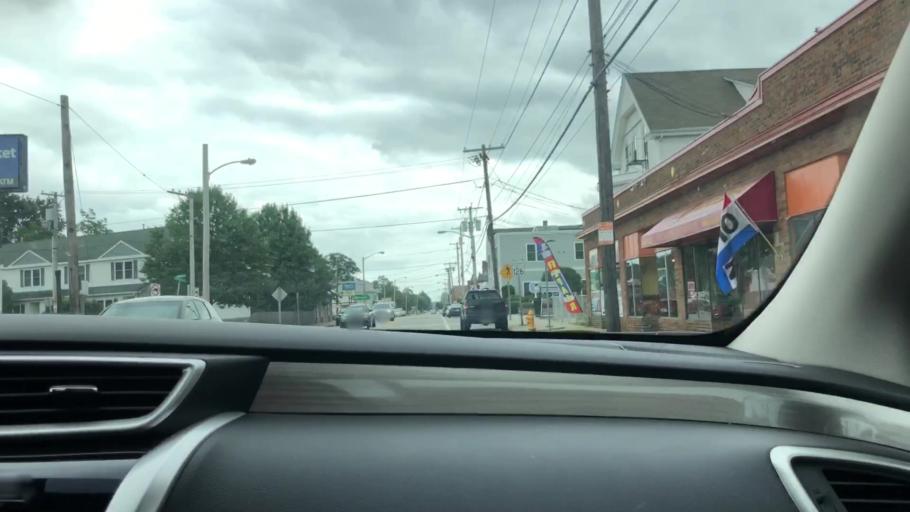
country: US
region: Rhode Island
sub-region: Providence County
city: Central Falls
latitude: 41.8785
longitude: -71.4154
